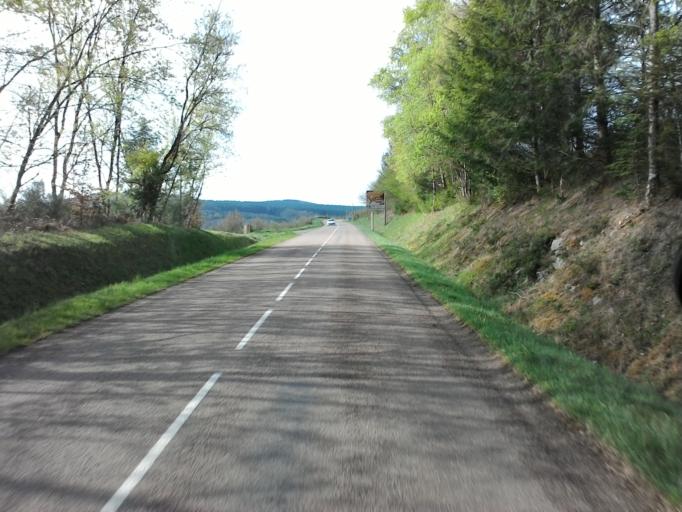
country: FR
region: Bourgogne
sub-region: Departement de la Nievre
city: Chateau-Chinon(Ville)
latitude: 47.2188
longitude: 4.0346
